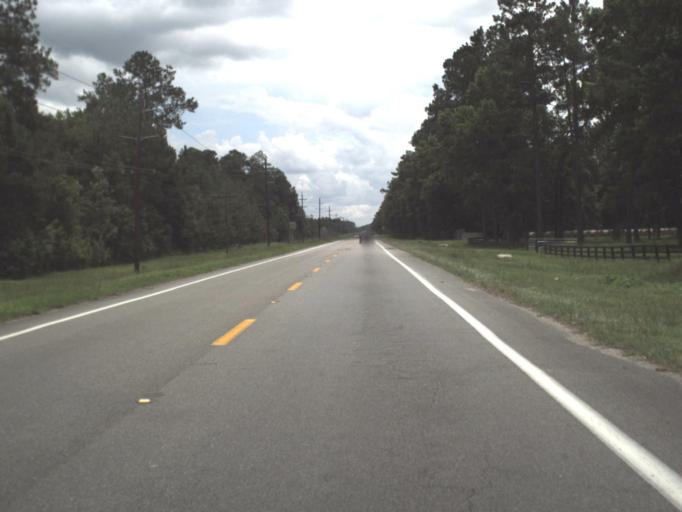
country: US
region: Florida
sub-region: Union County
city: Lake Butler
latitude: 30.0198
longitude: -82.3167
